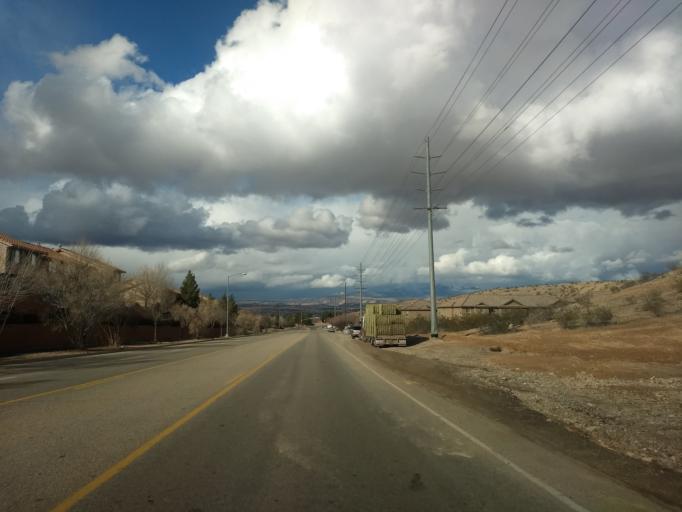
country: US
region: Utah
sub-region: Washington County
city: Saint George
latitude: 37.0480
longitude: -113.5553
